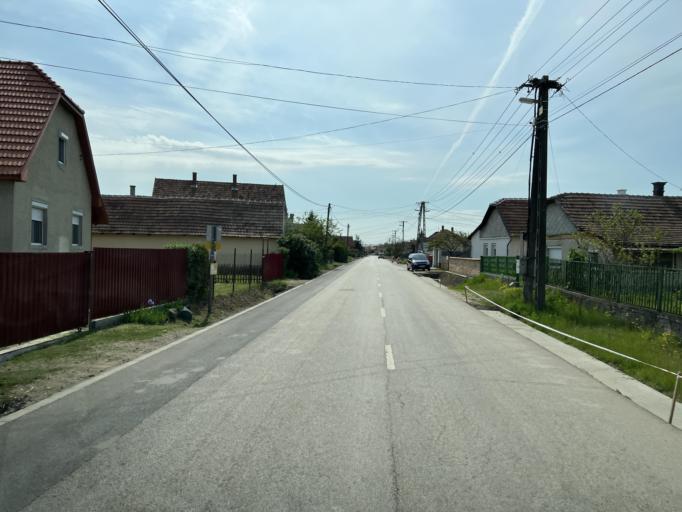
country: HU
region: Pest
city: Tapioszolos
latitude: 47.3000
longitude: 19.8273
